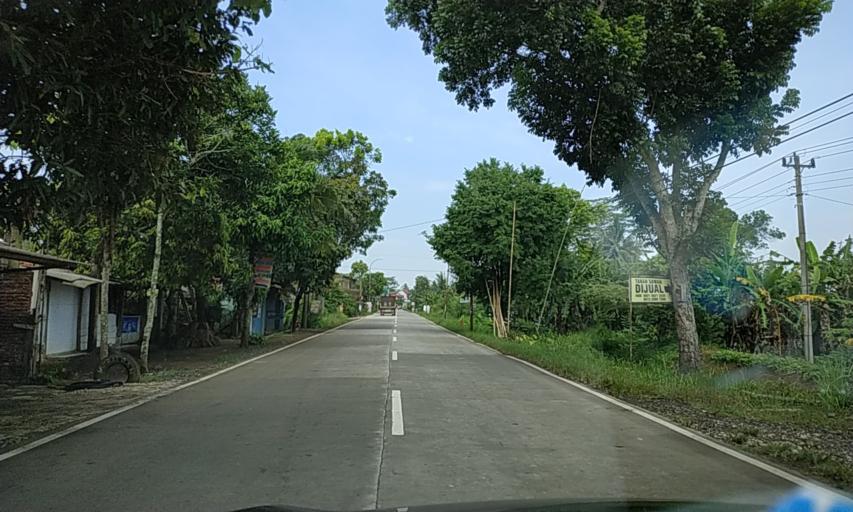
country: ID
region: Central Java
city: Tambangan
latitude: -7.4846
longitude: 108.8224
